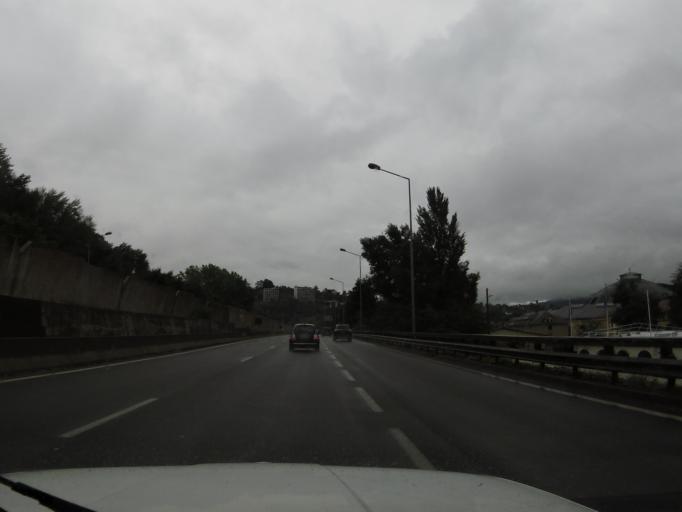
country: FR
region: Rhone-Alpes
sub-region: Departement de la Savoie
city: Chambery
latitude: 45.5796
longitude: 5.9149
